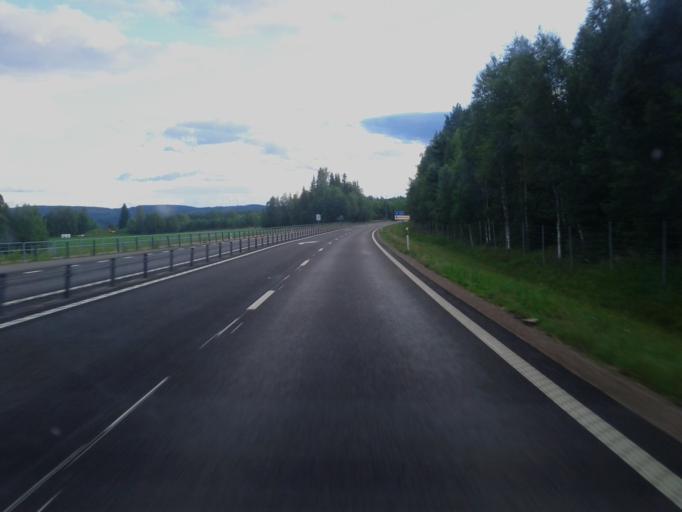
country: SE
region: Dalarna
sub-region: Borlange Kommun
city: Borlaenge
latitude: 60.4387
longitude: 15.3577
